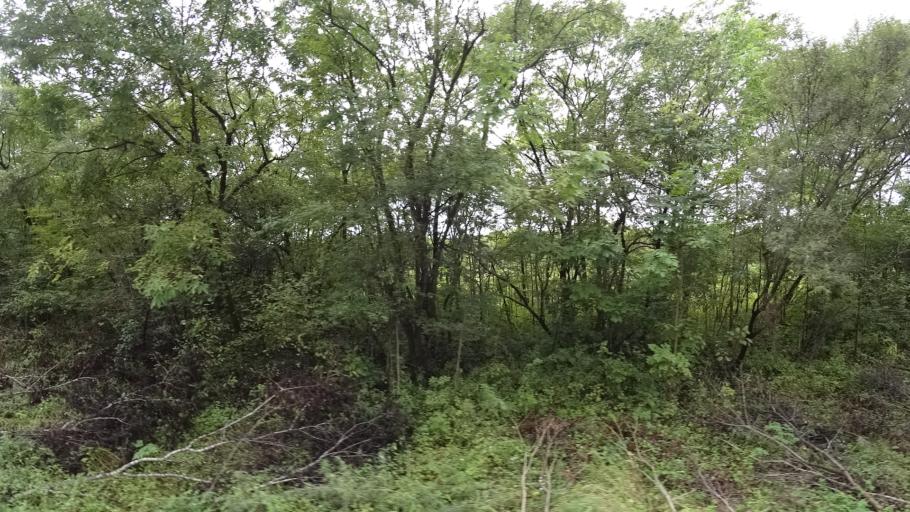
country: RU
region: Primorskiy
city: Lyalichi
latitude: 44.0779
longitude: 132.4546
